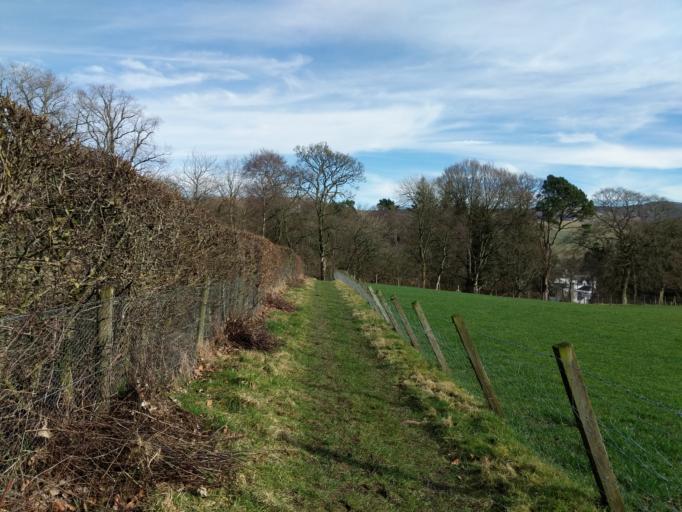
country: GB
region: Scotland
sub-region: The Scottish Borders
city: Peebles
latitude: 55.7132
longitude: -3.2219
